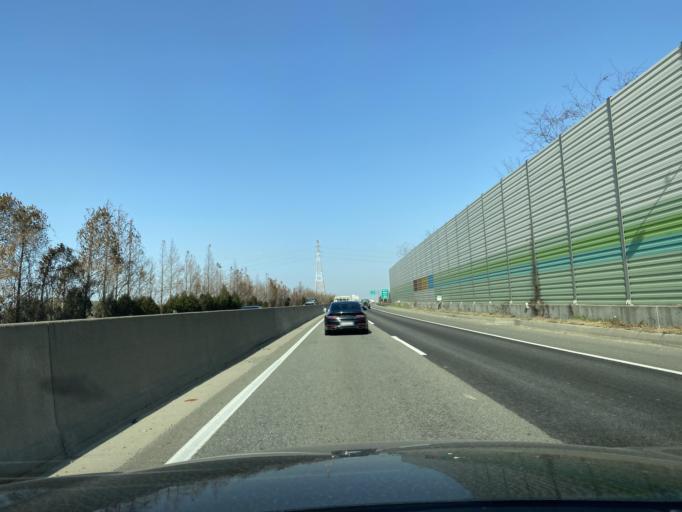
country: KR
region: Gyeonggi-do
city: Hwaseong-si
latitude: 37.2178
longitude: 126.7598
